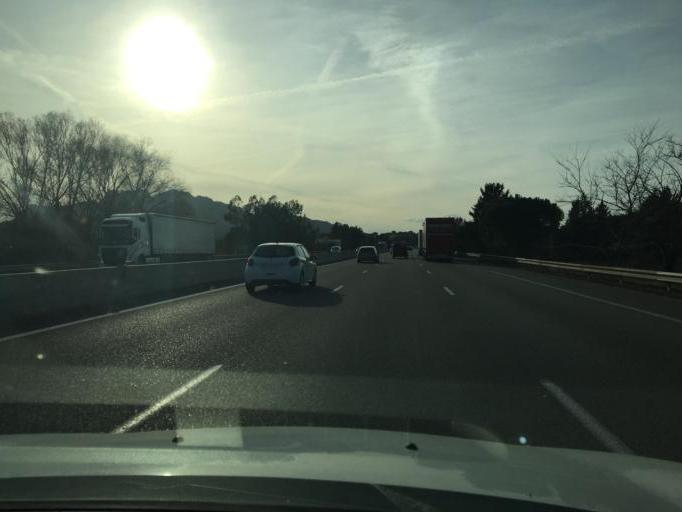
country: FR
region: Provence-Alpes-Cote d'Azur
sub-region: Departement du Var
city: Roquebrune-sur-Argens
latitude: 43.4646
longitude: 6.6404
